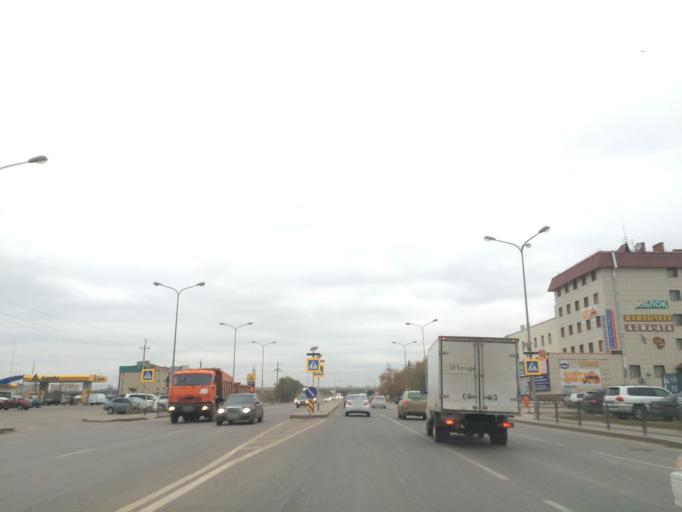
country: KZ
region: Astana Qalasy
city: Astana
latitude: 51.1837
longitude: 71.4538
